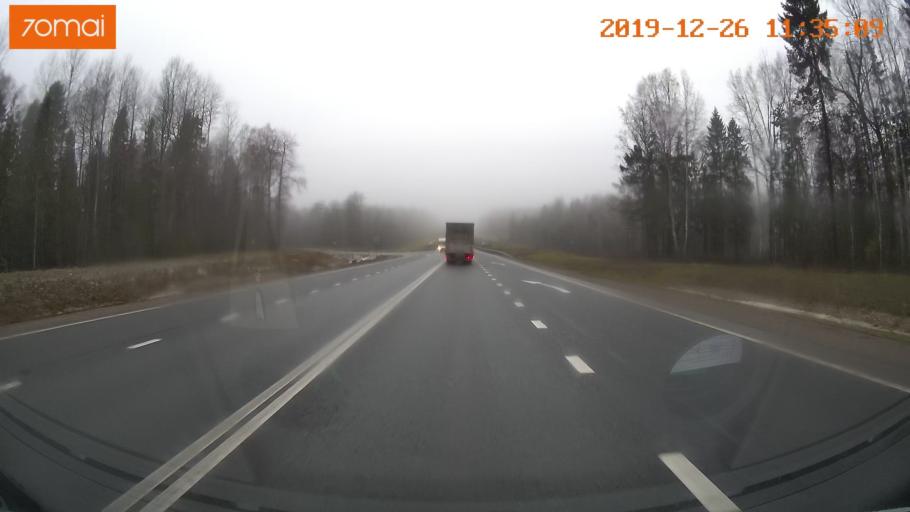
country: RU
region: Vologda
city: Chebsara
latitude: 59.1870
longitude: 38.6740
